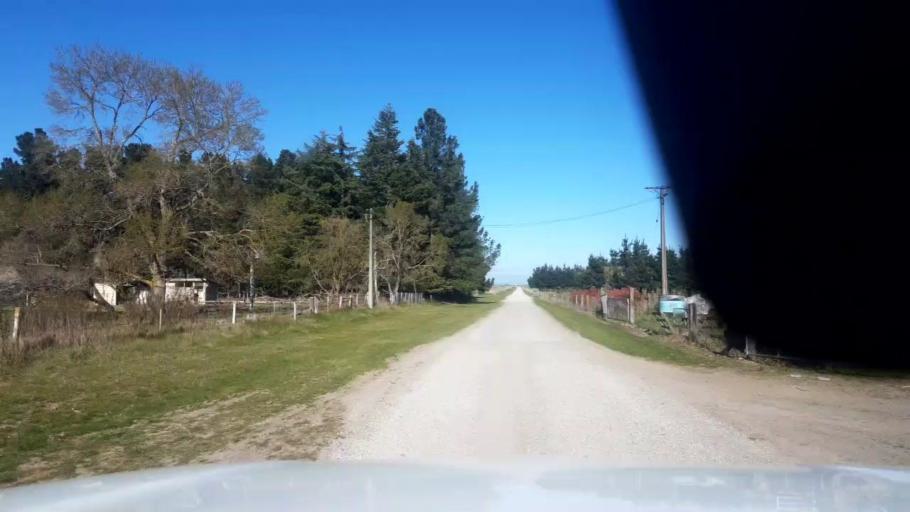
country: NZ
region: Canterbury
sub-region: Timaru District
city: Pleasant Point
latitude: -44.0681
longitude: 171.3708
